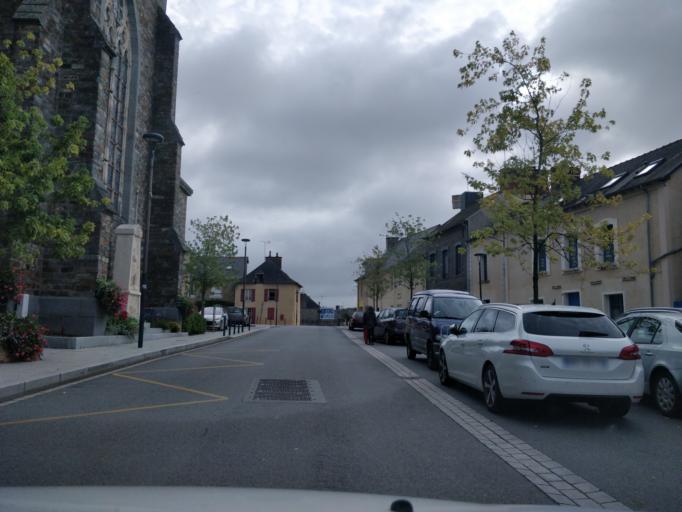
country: FR
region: Brittany
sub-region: Departement d'Ille-et-Vilaine
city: Servon-sur-Vilaine
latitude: 48.1212
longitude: -1.4602
